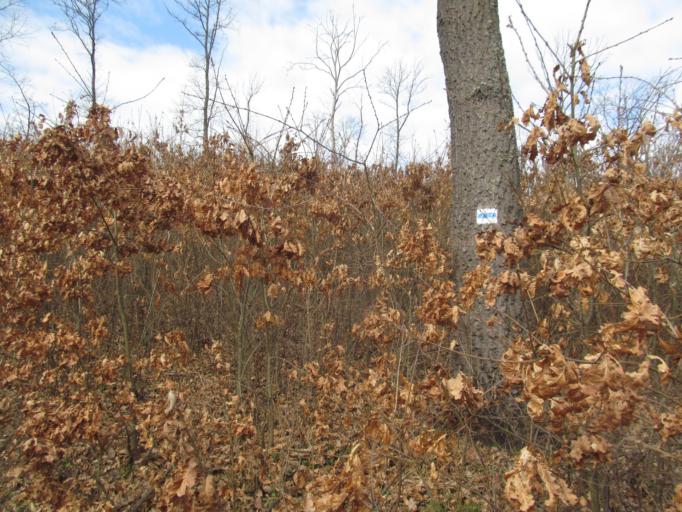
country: HU
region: Borsod-Abauj-Zemplen
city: Putnok
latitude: 48.3802
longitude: 20.4546
